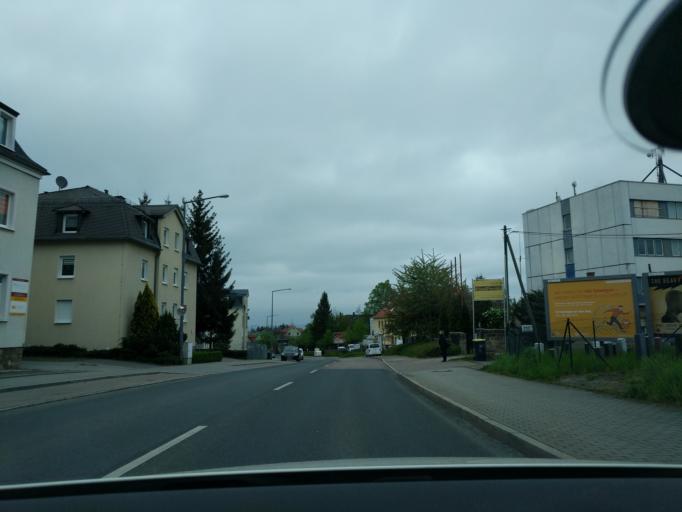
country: DE
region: Saxony
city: Bannewitz
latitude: 51.0072
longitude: 13.6896
